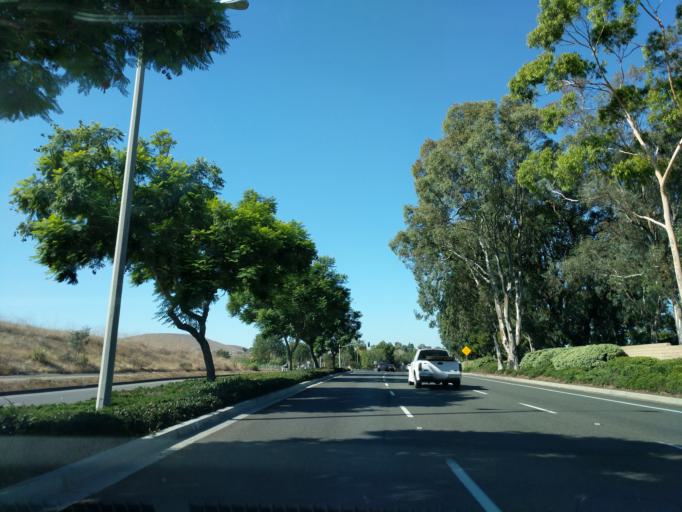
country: US
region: California
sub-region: Orange County
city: Irvine
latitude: 33.6591
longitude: -117.8000
